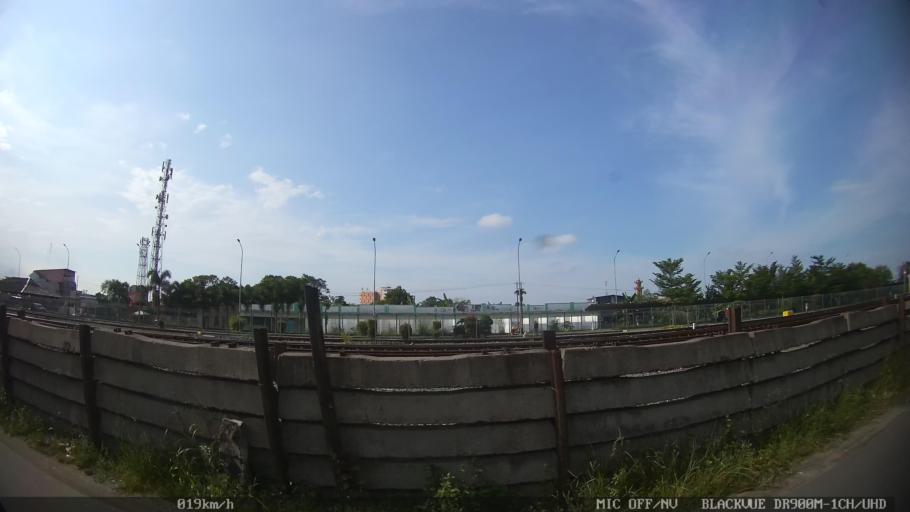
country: ID
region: North Sumatra
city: Medan
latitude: 3.5937
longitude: 98.7561
